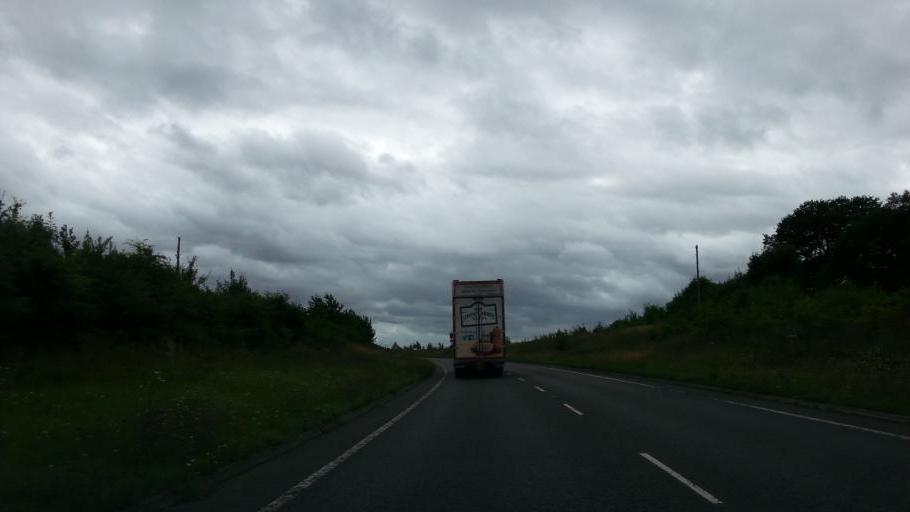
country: GB
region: England
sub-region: Cambridgeshire
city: Papworth Everard
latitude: 52.2487
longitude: -0.1290
